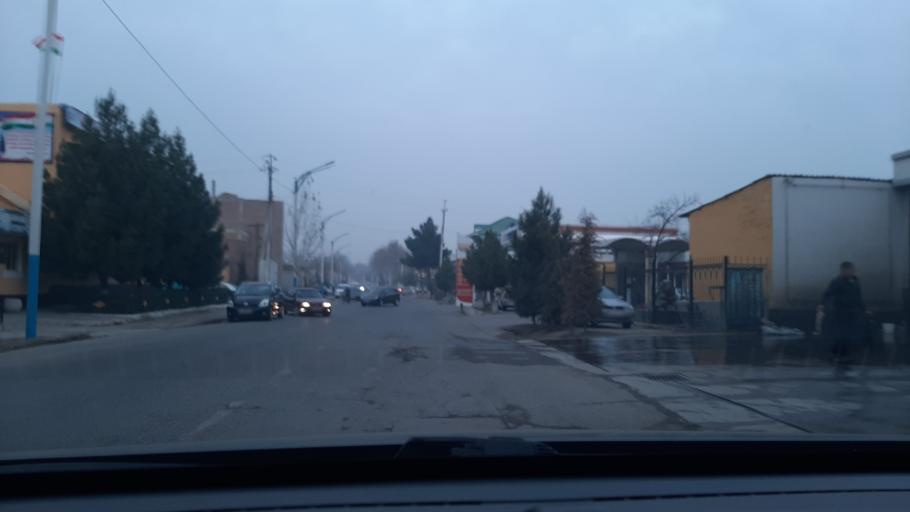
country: TJ
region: Viloyati Sughd
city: Khujand
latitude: 40.2690
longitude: 69.6026
